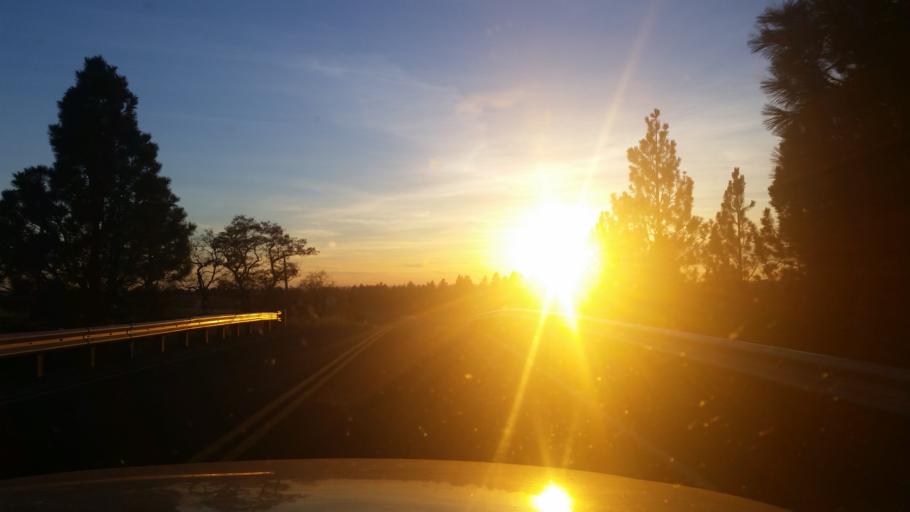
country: US
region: Washington
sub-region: Spokane County
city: Veradale
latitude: 47.5069
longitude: -117.1526
